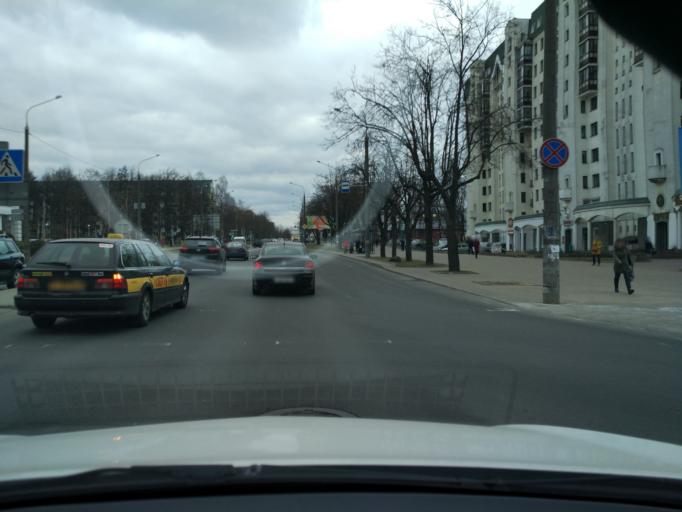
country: BY
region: Minsk
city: Minsk
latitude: 53.9328
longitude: 27.5901
